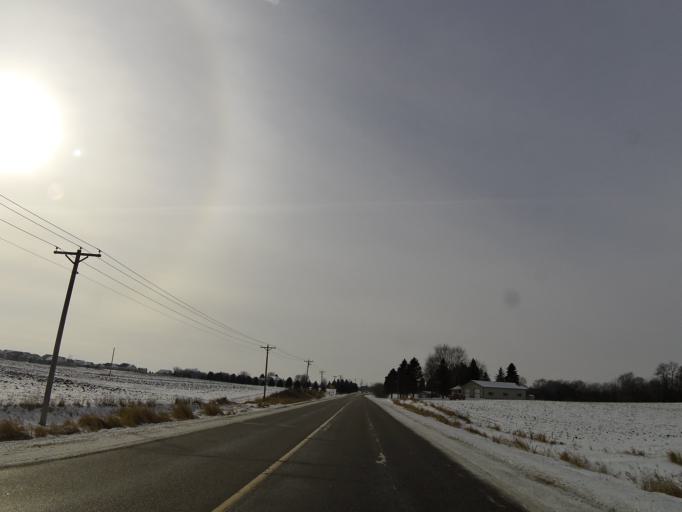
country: US
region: Minnesota
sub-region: Carver County
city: Mayer
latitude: 44.8986
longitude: -93.8762
